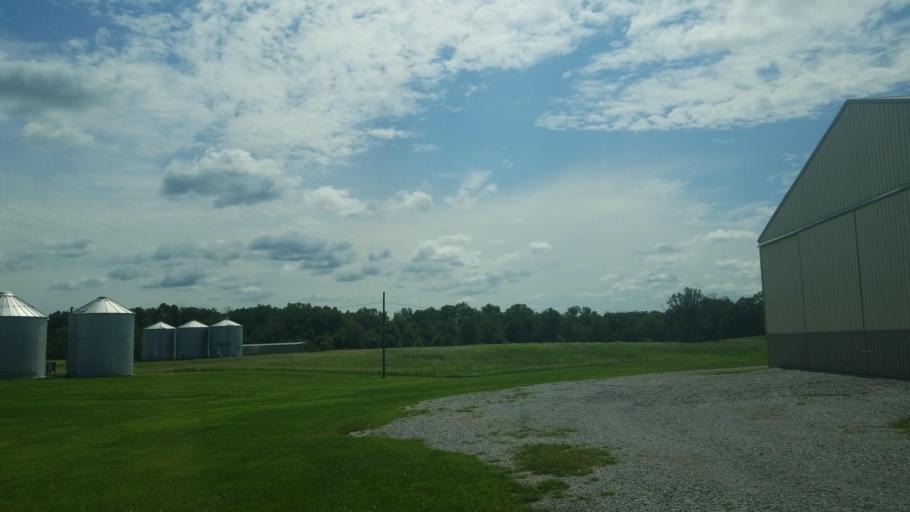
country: US
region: Illinois
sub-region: Williamson County
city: Johnston City
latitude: 37.7904
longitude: -88.7687
